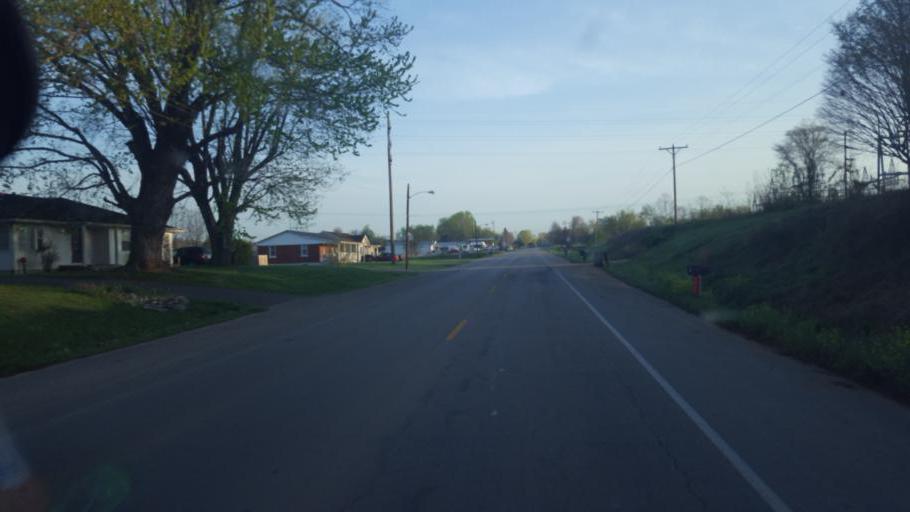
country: US
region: Kentucky
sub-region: Hart County
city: Munfordville
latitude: 37.3827
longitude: -85.9035
